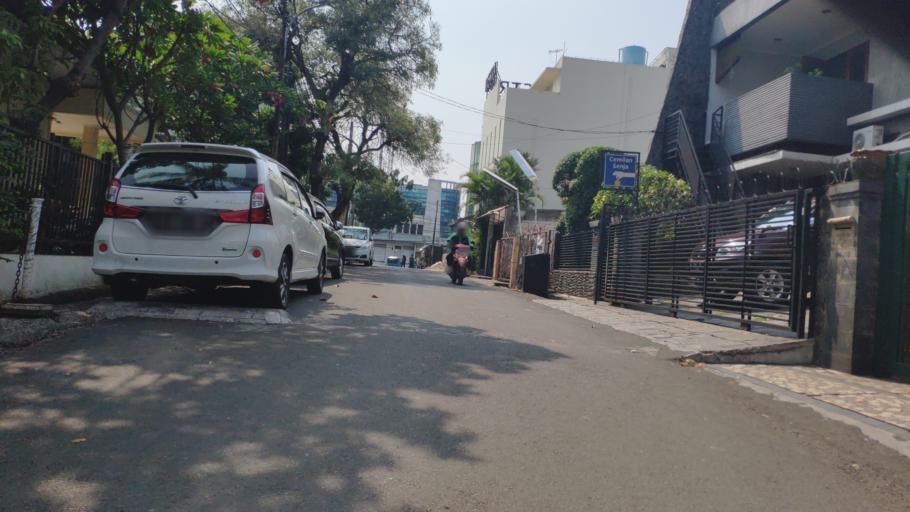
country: ID
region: Jakarta Raya
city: Jakarta
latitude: -6.2506
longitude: 106.7924
